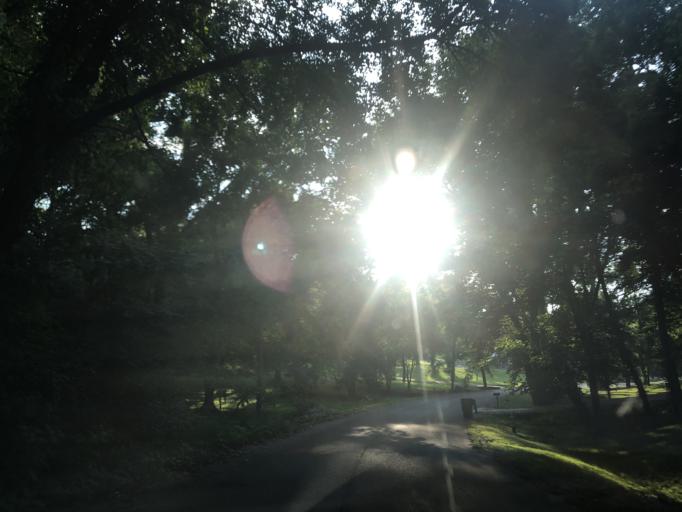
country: US
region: Tennessee
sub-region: Davidson County
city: Nashville
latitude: 36.1686
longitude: -86.7031
